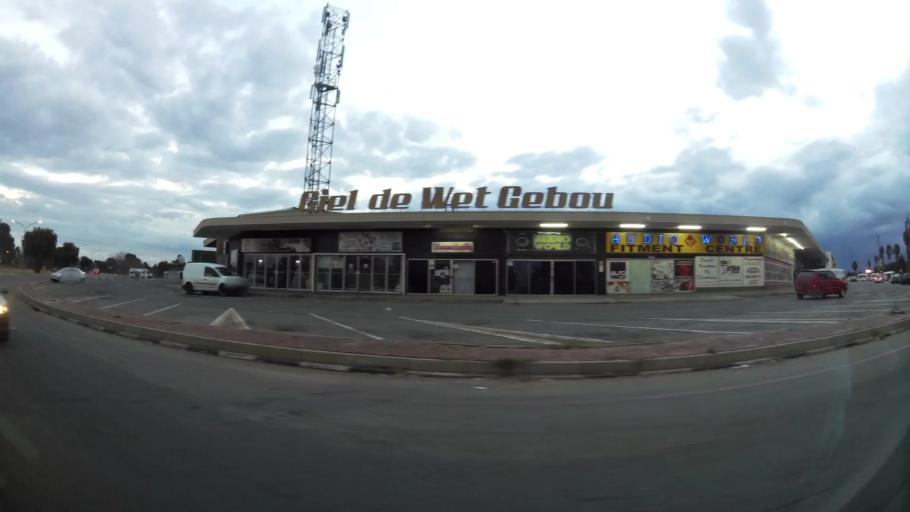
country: ZA
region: Orange Free State
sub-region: Lejweleputswa District Municipality
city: Welkom
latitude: -27.9822
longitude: 26.7418
